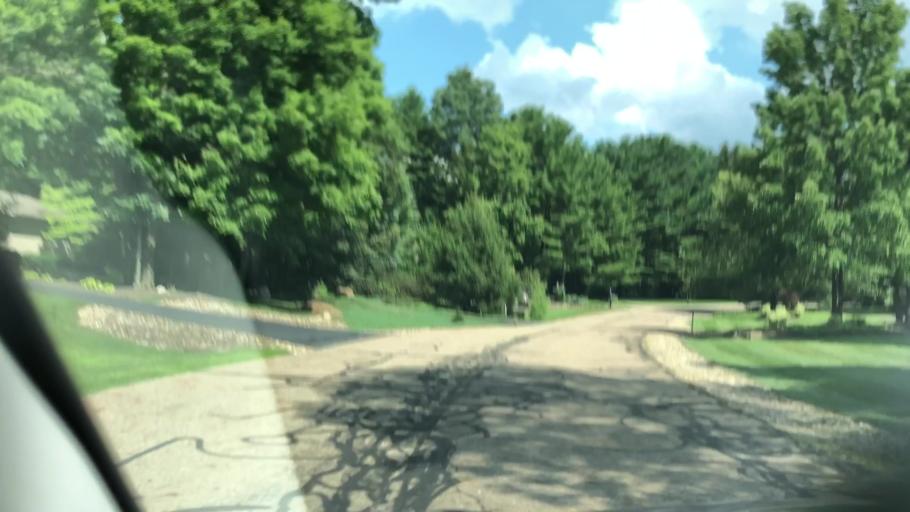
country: US
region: Ohio
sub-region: Summit County
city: Montrose-Ghent
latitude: 41.1640
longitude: -81.6437
